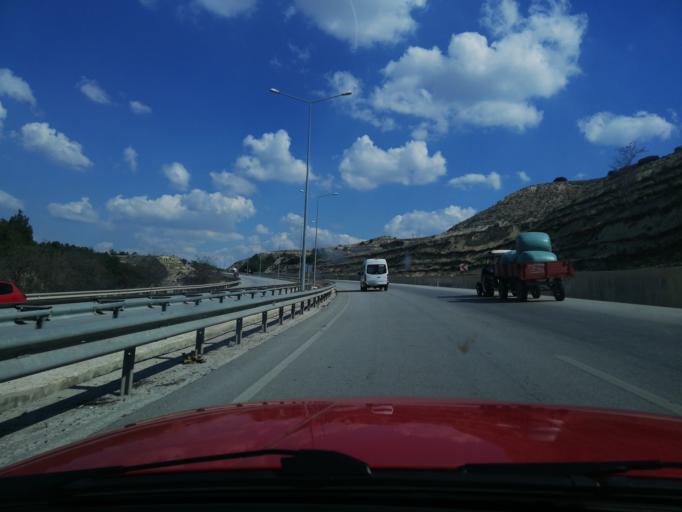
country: TR
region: Burdur
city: Burdur
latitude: 37.7013
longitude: 30.3091
